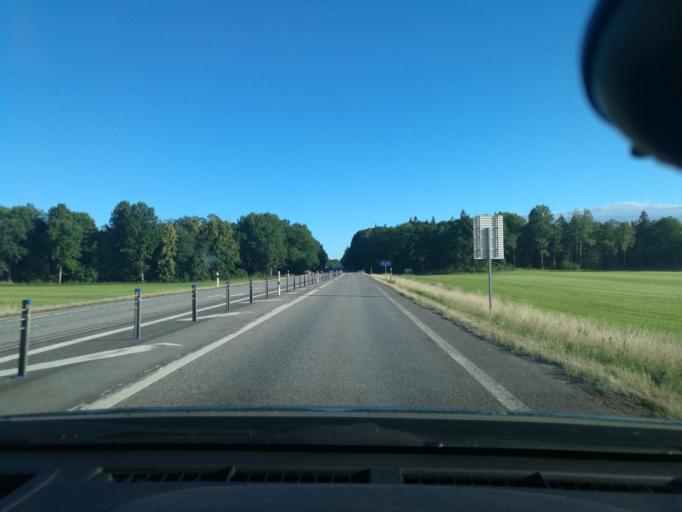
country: SE
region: Kalmar
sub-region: Monsteras Kommun
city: Timmernabben
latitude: 56.9529
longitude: 16.3900
